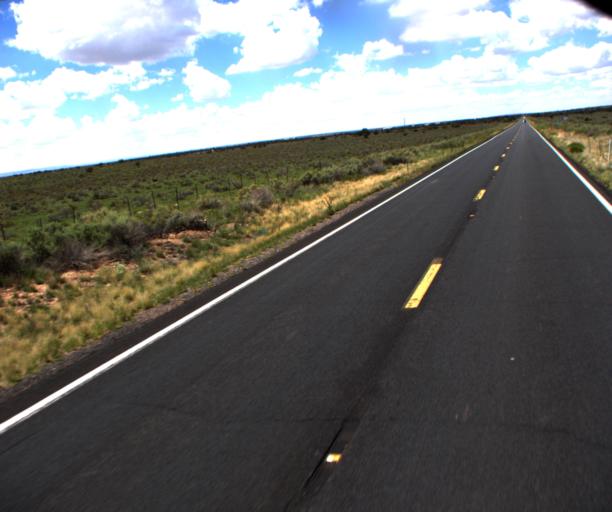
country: US
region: Arizona
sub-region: Coconino County
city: Williams
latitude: 35.6316
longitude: -112.1185
